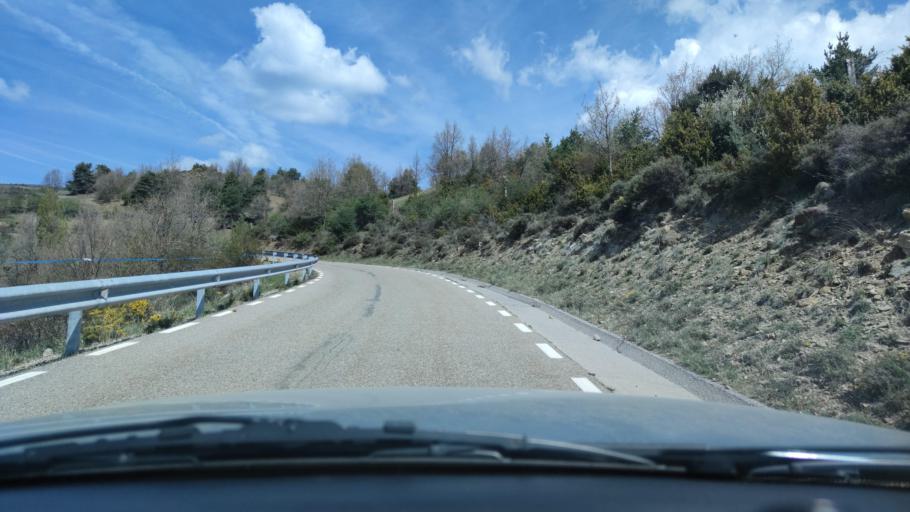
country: ES
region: Catalonia
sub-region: Provincia de Lleida
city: Coll de Nargo
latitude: 42.2906
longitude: 1.2444
